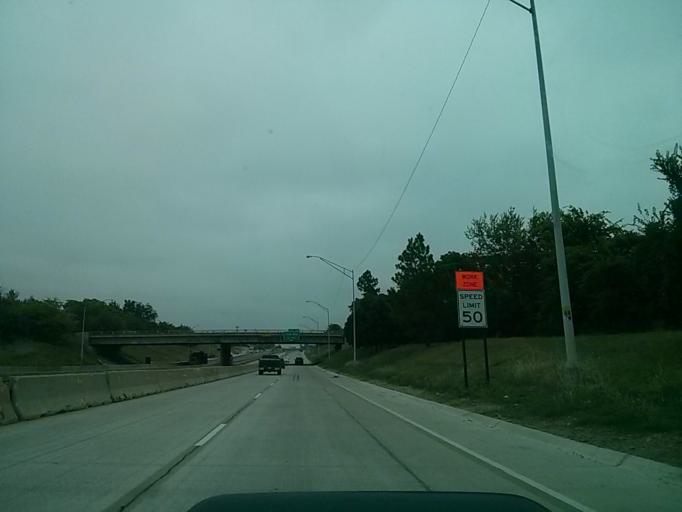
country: US
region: Oklahoma
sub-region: Tulsa County
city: Tulsa
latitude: 36.1593
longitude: -95.9332
